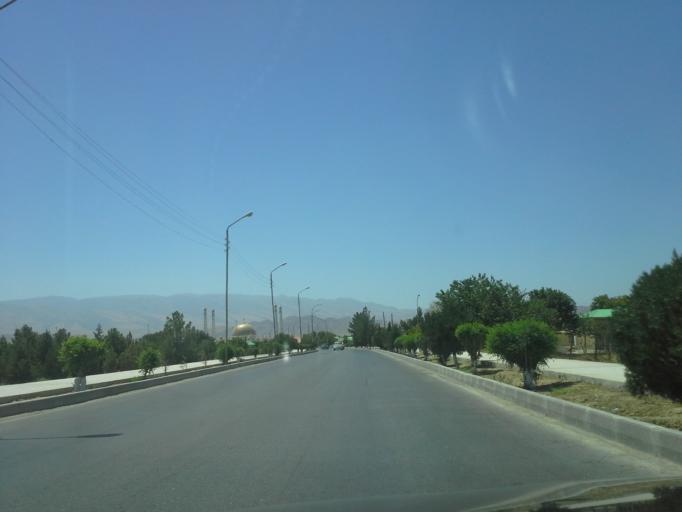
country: TM
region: Ahal
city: Abadan
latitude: 38.0280
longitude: 58.2617
